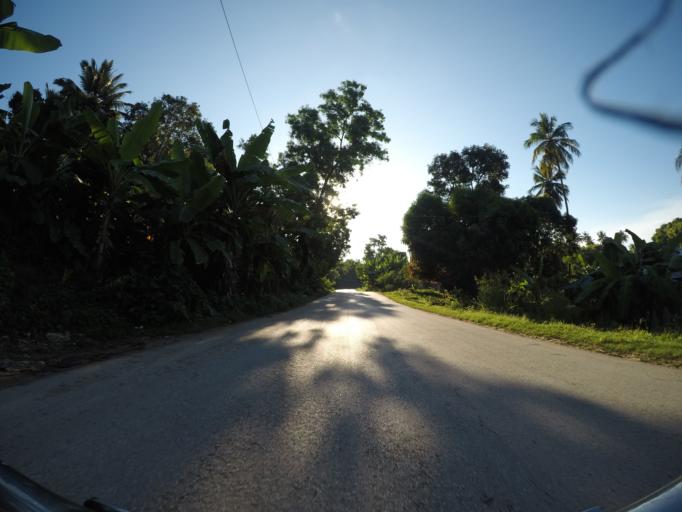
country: TZ
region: Pemba South
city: Mtambile
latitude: -5.3802
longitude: 39.6971
